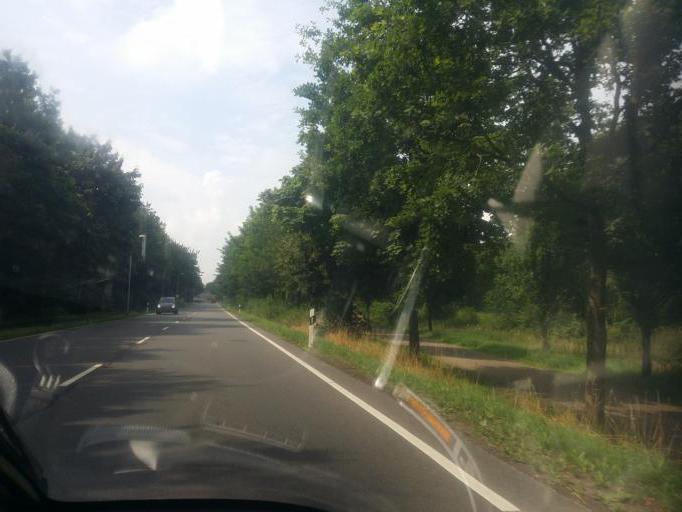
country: DE
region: Schleswig-Holstein
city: Heide
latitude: 54.2046
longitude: 9.1143
